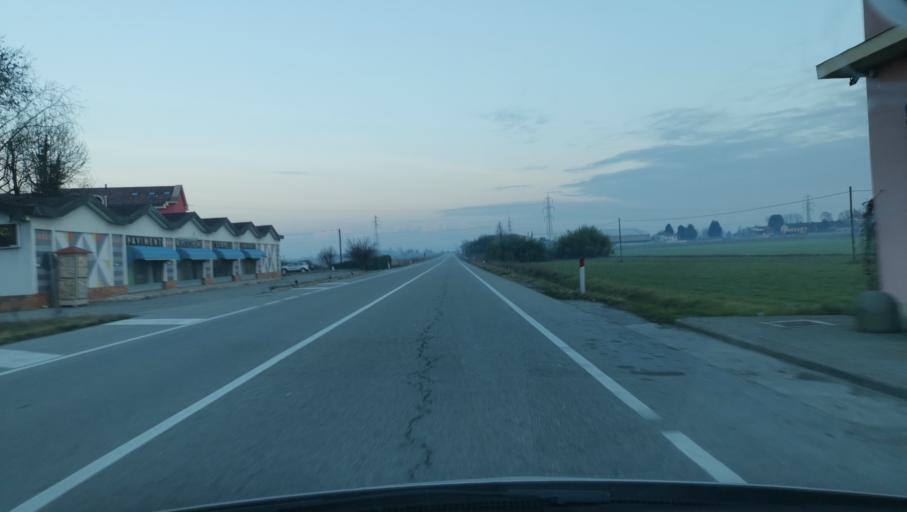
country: IT
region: Piedmont
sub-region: Provincia di Torino
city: Chivasso
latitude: 45.2197
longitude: 7.8906
